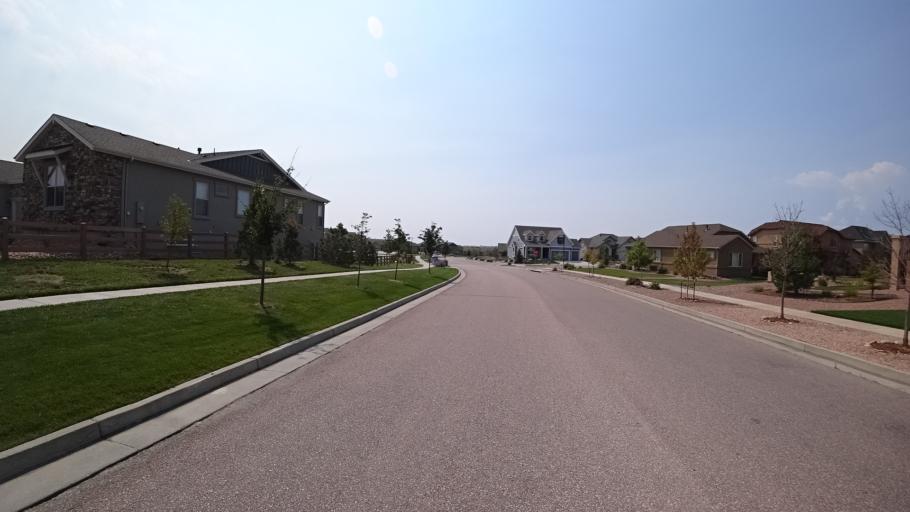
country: US
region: Colorado
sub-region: El Paso County
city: Black Forest
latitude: 38.9674
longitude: -104.7140
